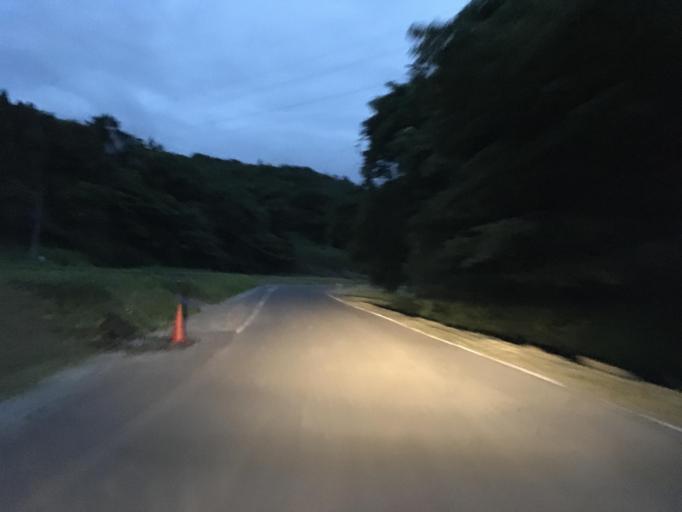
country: JP
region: Miyagi
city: Furukawa
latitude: 38.7864
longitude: 140.9399
